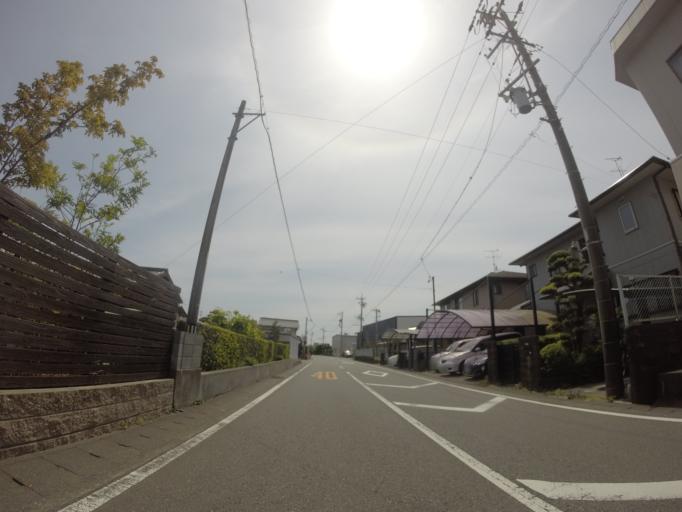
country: JP
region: Shizuoka
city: Fujieda
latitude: 34.8195
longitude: 138.2722
